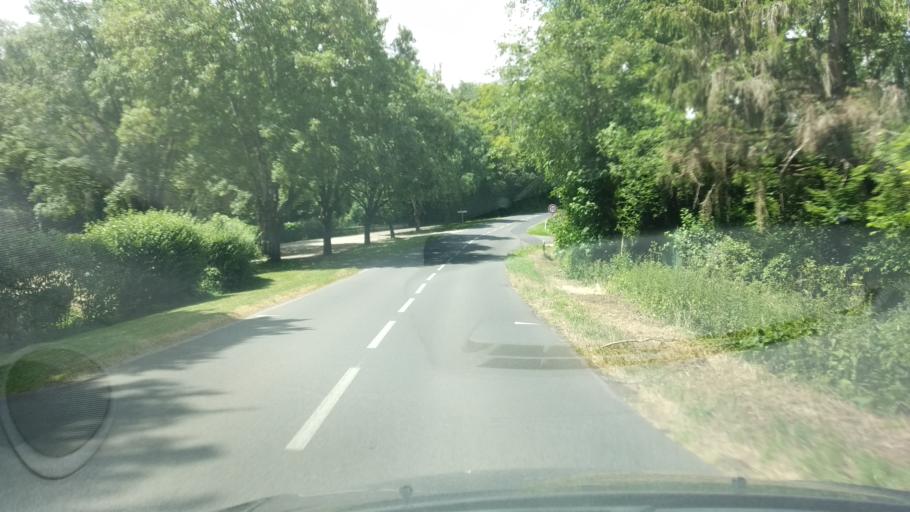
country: FR
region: Poitou-Charentes
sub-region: Departement de la Vienne
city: Cisse
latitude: 46.6174
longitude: 0.2154
